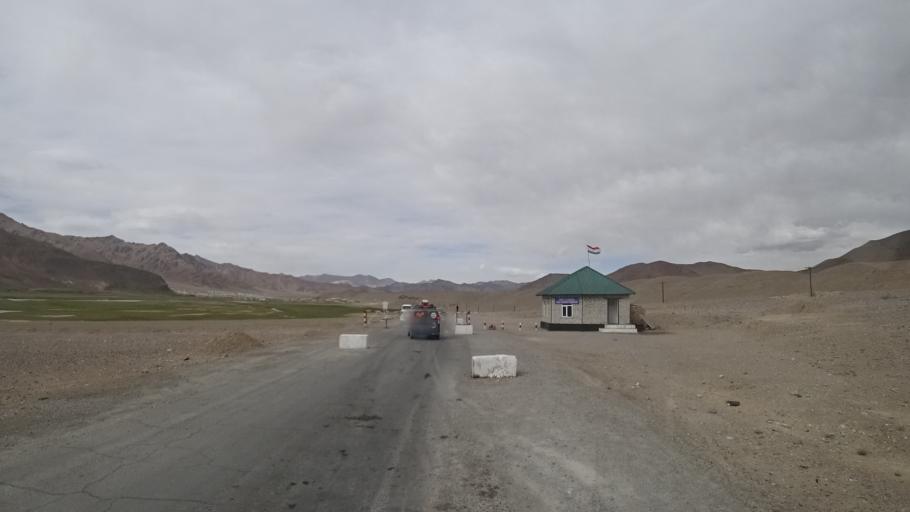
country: TJ
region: Gorno-Badakhshan
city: Murghob
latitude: 38.1314
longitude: 73.9516
